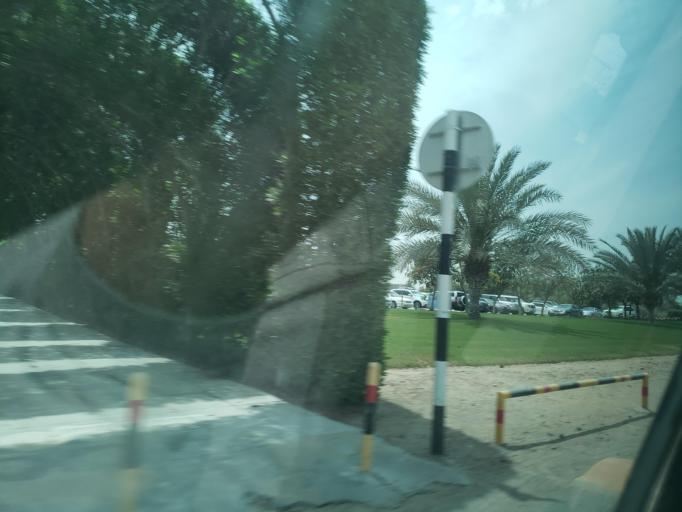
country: AE
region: Ash Shariqah
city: Sharjah
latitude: 25.3215
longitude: 55.5154
